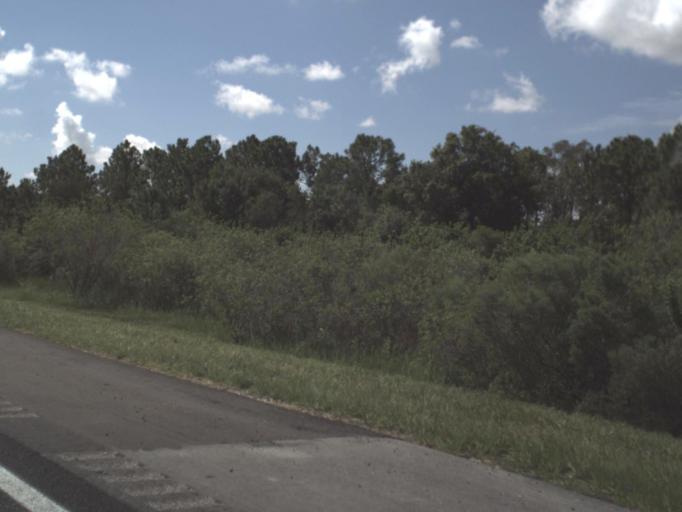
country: US
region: Florida
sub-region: Lee County
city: Suncoast Estates
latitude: 26.7587
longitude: -81.8724
